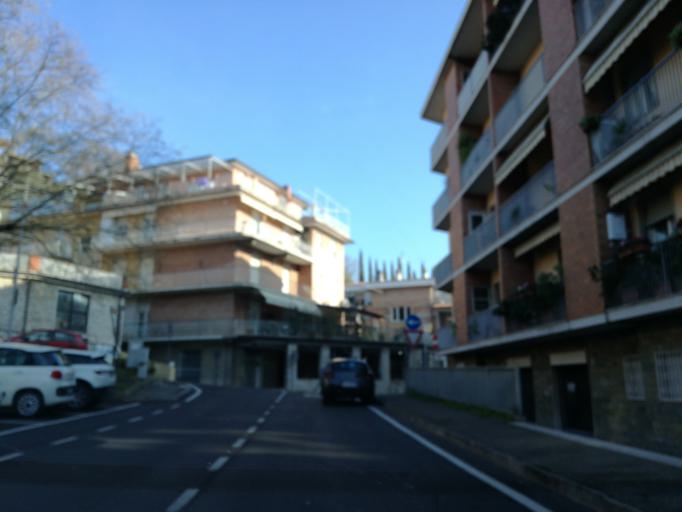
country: IT
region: Umbria
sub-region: Provincia di Perugia
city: Perugia
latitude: 43.1081
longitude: 12.3749
